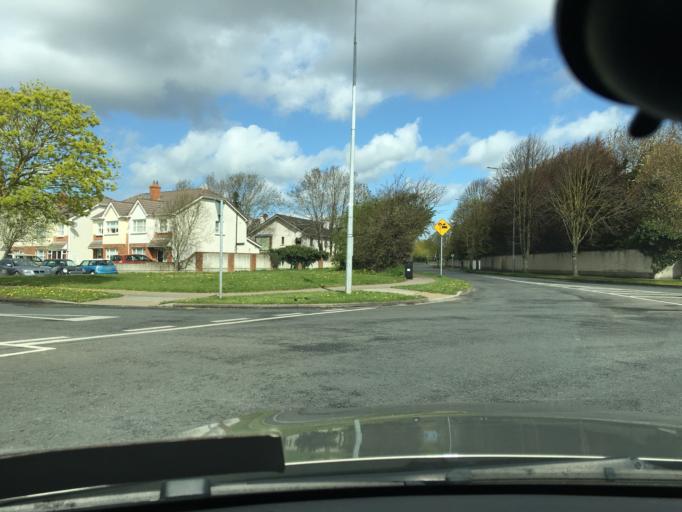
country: IE
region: Leinster
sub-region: Fingal County
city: Blanchardstown
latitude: 53.3755
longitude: -6.3911
